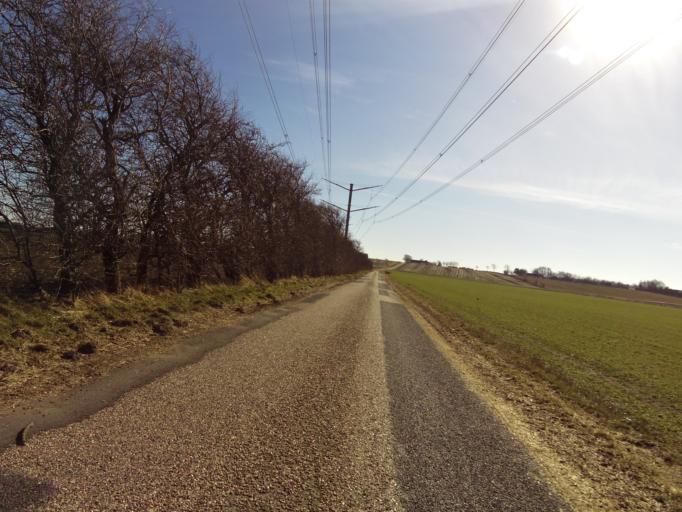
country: DK
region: South Denmark
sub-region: Tonder Kommune
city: Toftlund
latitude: 55.2176
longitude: 9.1488
